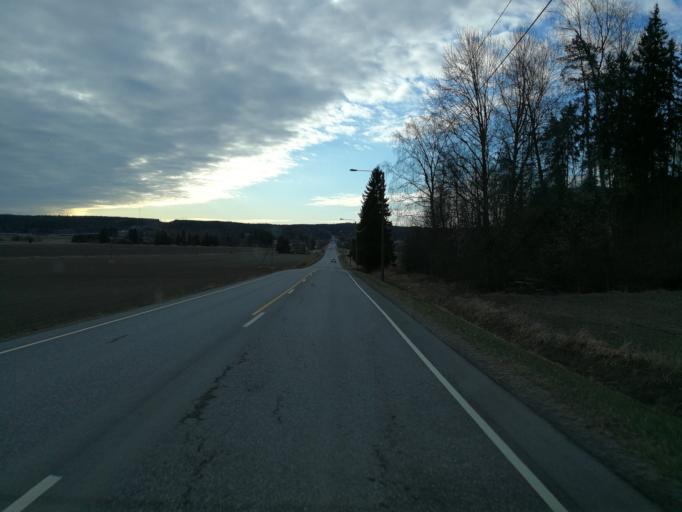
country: FI
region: Varsinais-Suomi
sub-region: Turku
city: Paimio
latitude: 60.4234
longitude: 22.6429
